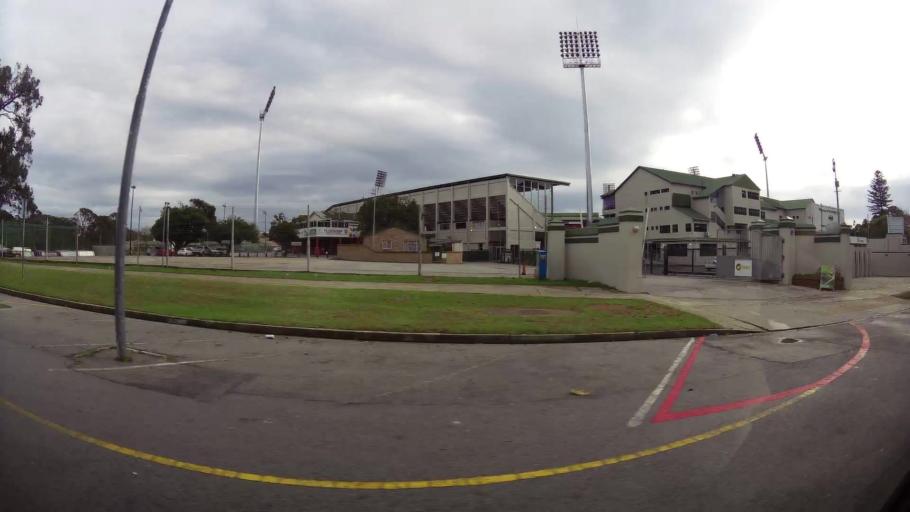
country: ZA
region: Eastern Cape
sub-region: Nelson Mandela Bay Metropolitan Municipality
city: Port Elizabeth
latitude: -33.9680
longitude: 25.6103
